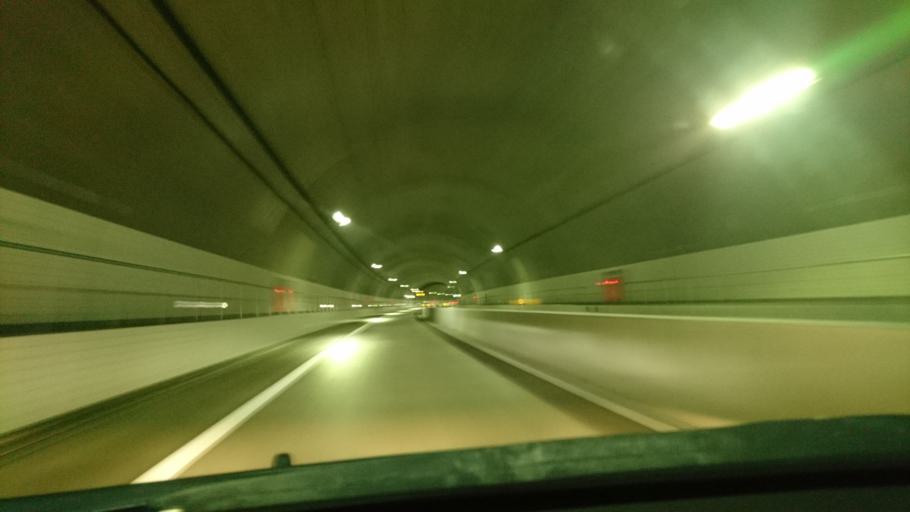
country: JP
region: Iwate
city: Miyako
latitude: 39.8131
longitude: 141.9584
